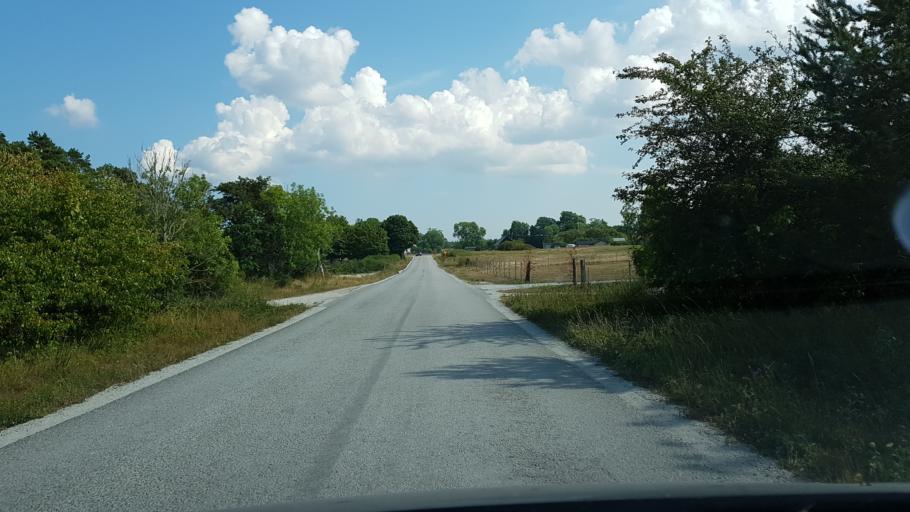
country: SE
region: Gotland
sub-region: Gotland
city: Visby
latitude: 57.8131
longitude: 18.5250
